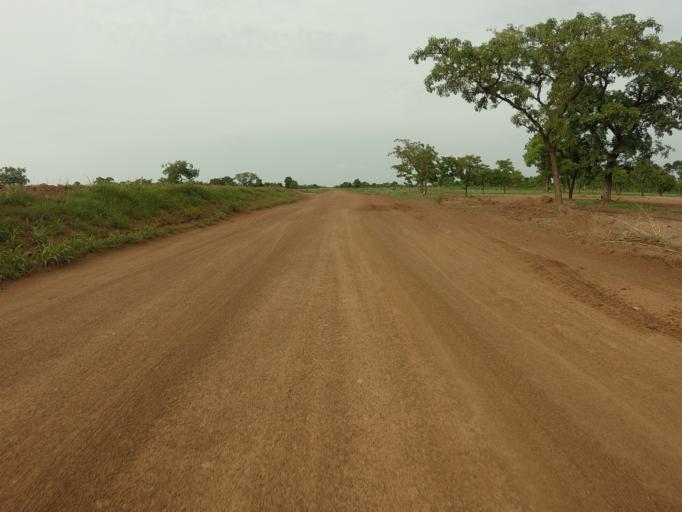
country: GH
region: Northern
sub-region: Yendi
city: Yendi
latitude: 9.7896
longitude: -0.1158
